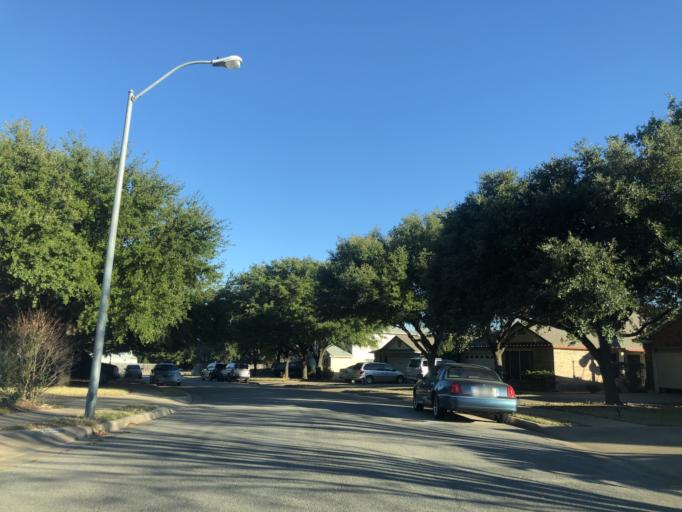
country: US
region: Texas
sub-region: Travis County
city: Windemere
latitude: 30.4807
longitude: -97.6563
